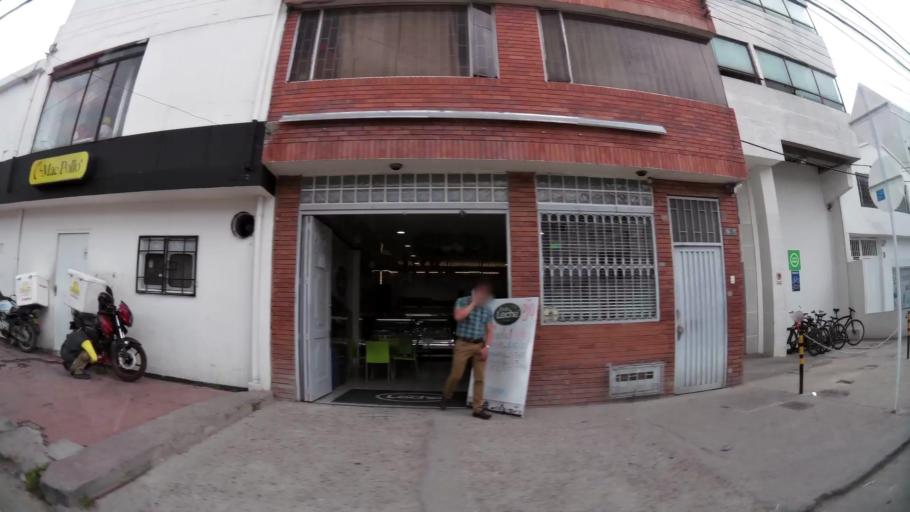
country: CO
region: Cundinamarca
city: La Calera
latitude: 4.7472
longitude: -74.0453
